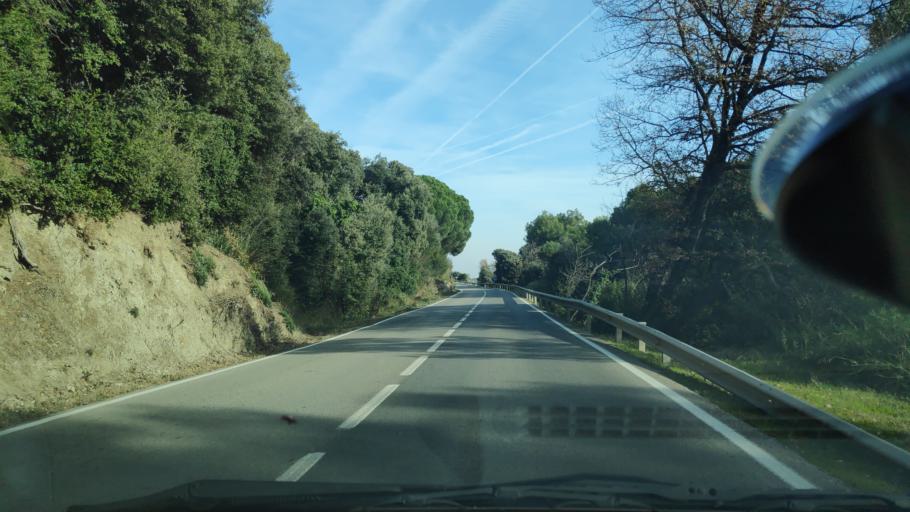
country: ES
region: Catalonia
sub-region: Provincia de Barcelona
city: Castellar del Valles
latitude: 41.6025
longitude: 2.0641
